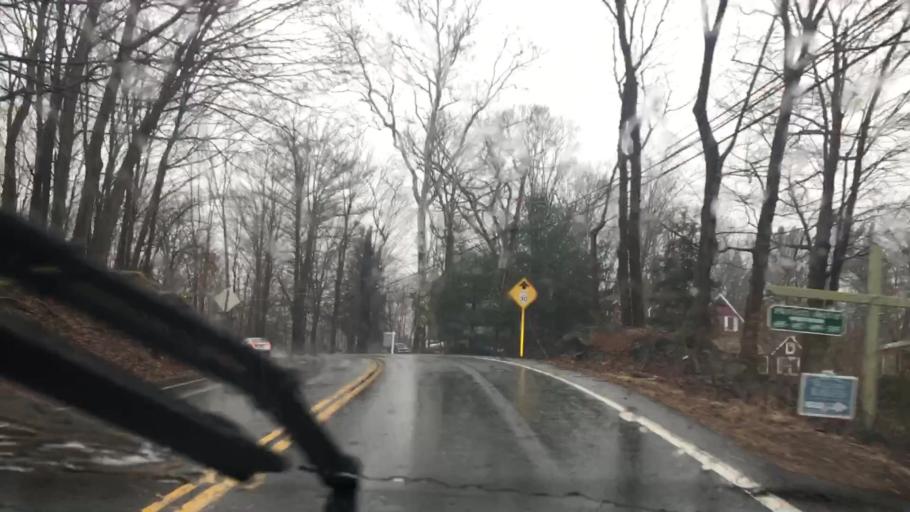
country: US
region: New York
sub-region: Putnam County
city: Putnam Lake
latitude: 41.4587
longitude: -73.5553
